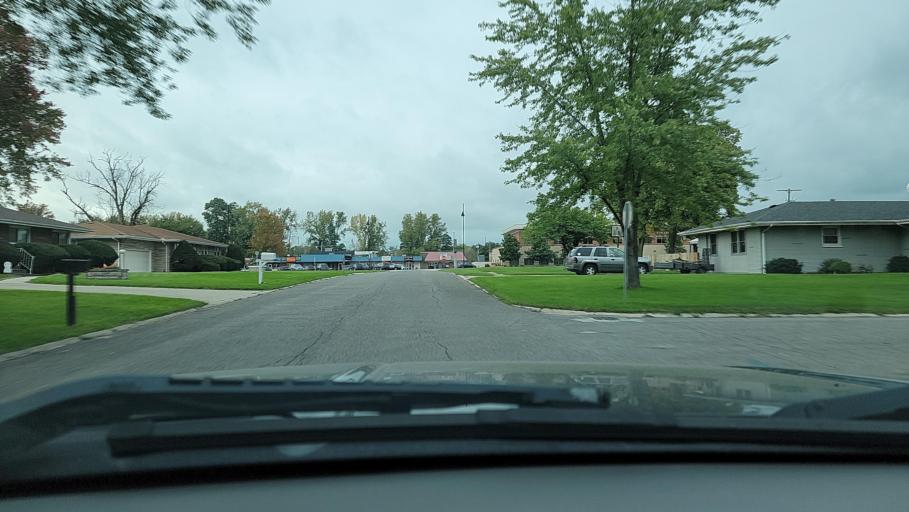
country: US
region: Indiana
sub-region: Porter County
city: Portage
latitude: 41.5747
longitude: -87.1739
